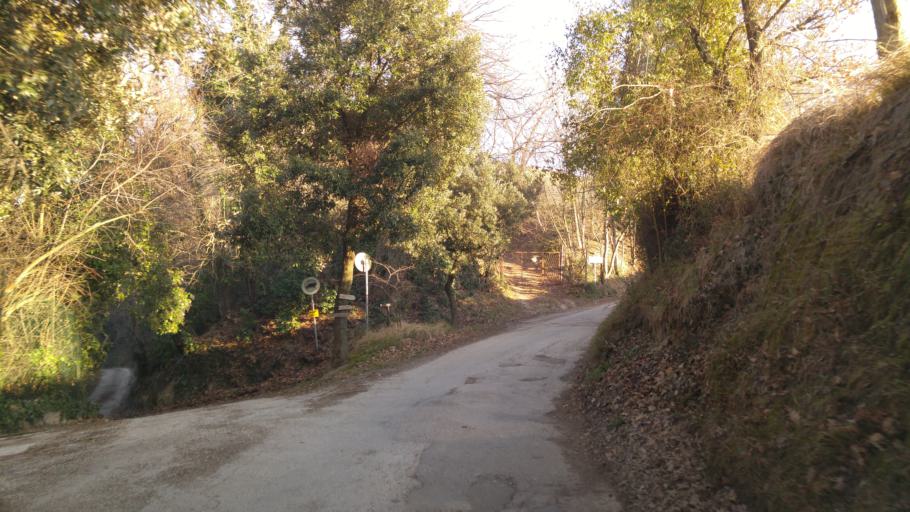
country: IT
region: The Marches
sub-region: Provincia di Pesaro e Urbino
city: Fenile
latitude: 43.8641
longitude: 12.9495
